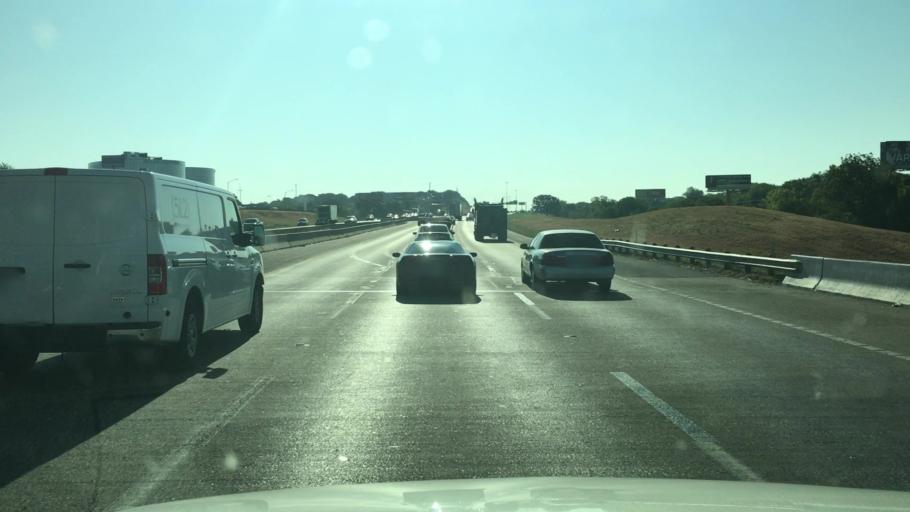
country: US
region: Texas
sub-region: Tarrant County
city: Haltom City
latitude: 32.7605
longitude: -97.2395
